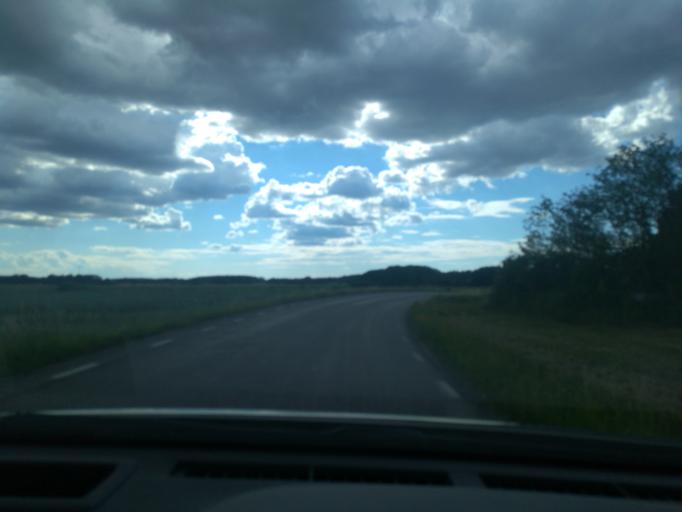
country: SE
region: Soedermanland
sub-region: Eskilstuna Kommun
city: Arla
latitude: 59.4476
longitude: 16.7499
